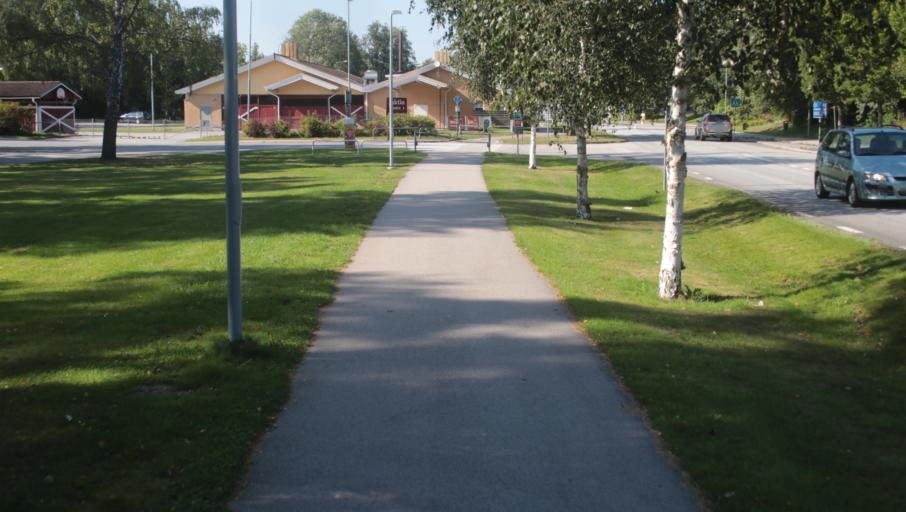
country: SE
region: Blekinge
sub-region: Karlshamns Kommun
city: Svangsta
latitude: 56.2591
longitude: 14.7728
